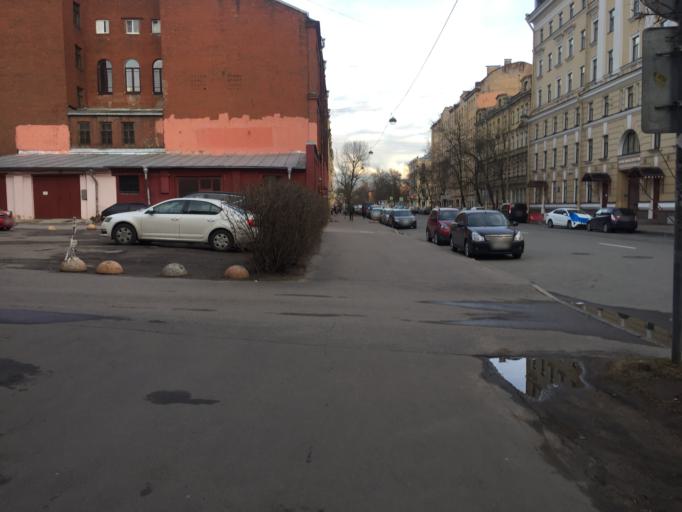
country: RU
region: St.-Petersburg
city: Vasyl'evsky Ostrov
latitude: 59.9483
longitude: 30.2728
